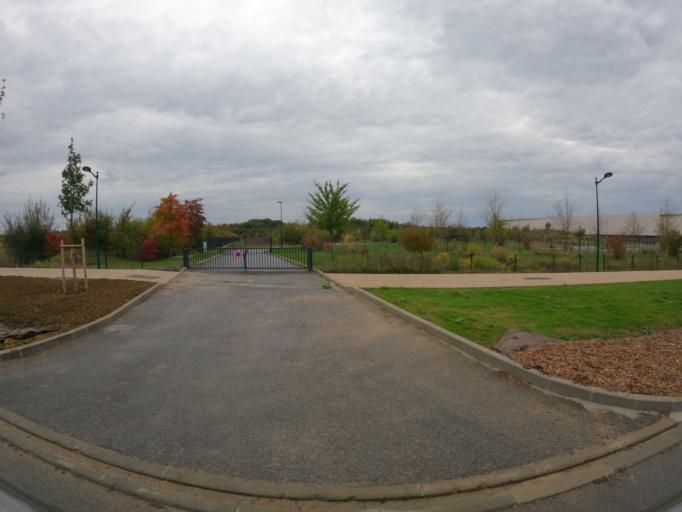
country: FR
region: Ile-de-France
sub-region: Departement de Seine-et-Marne
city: Serris
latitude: 48.8375
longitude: 2.8040
